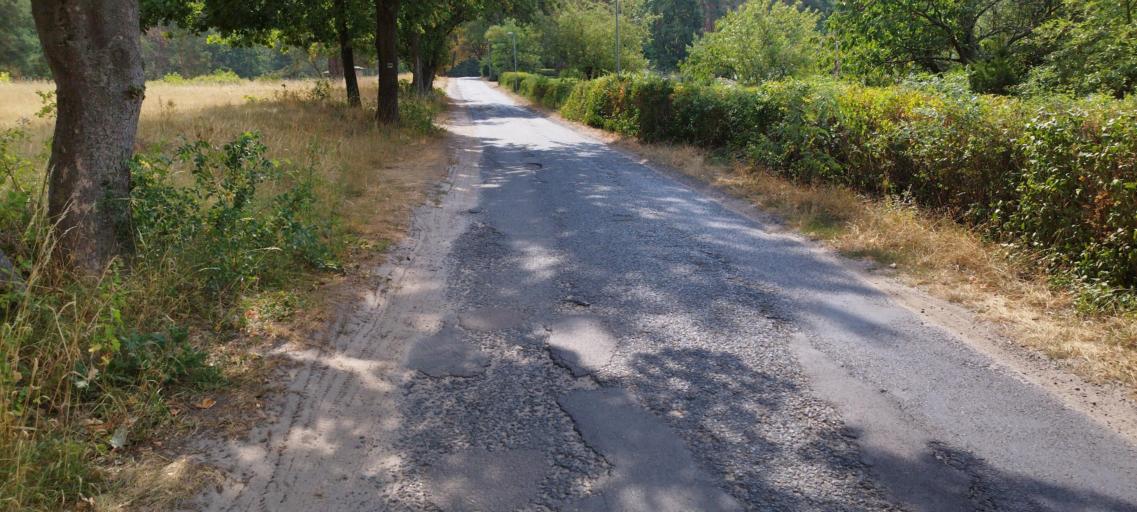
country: DE
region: Brandenburg
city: Strausberg
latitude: 52.5622
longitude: 13.8869
